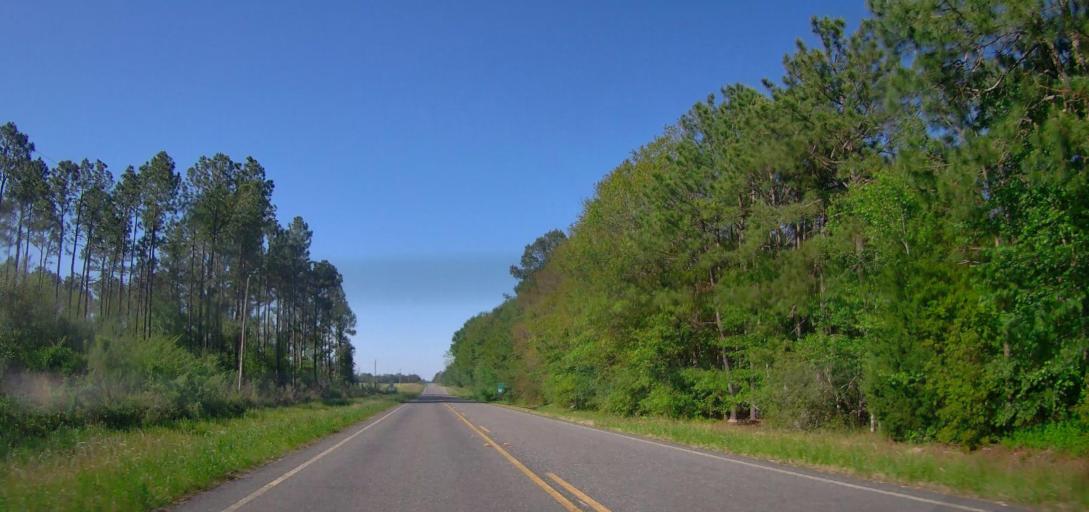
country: US
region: Georgia
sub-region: Wilcox County
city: Rochelle
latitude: 32.0507
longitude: -83.5036
